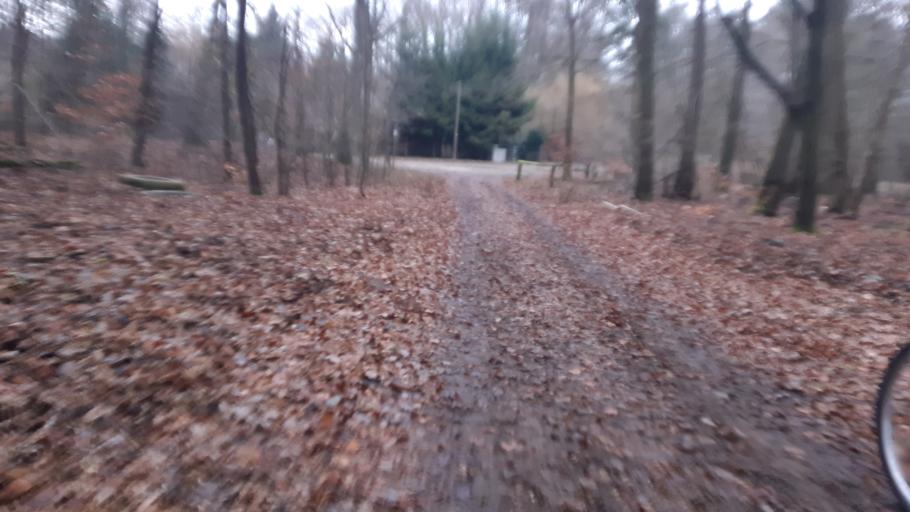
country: DE
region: Brandenburg
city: Templin
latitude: 53.1068
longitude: 13.5335
